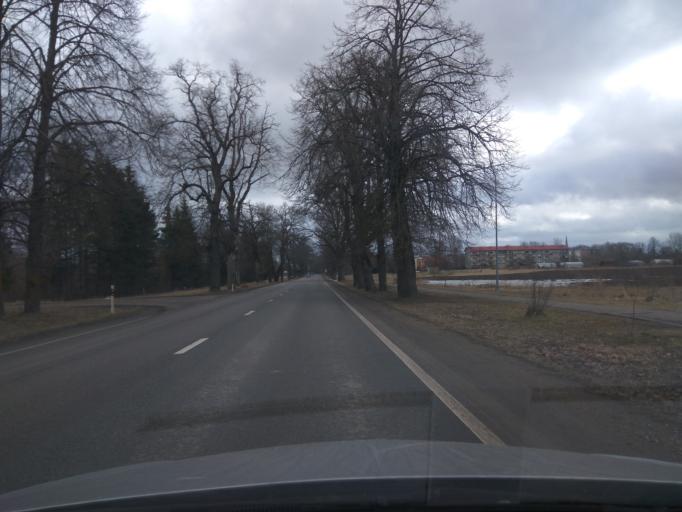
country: LV
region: Kuldigas Rajons
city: Kuldiga
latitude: 57.2753
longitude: 22.0293
